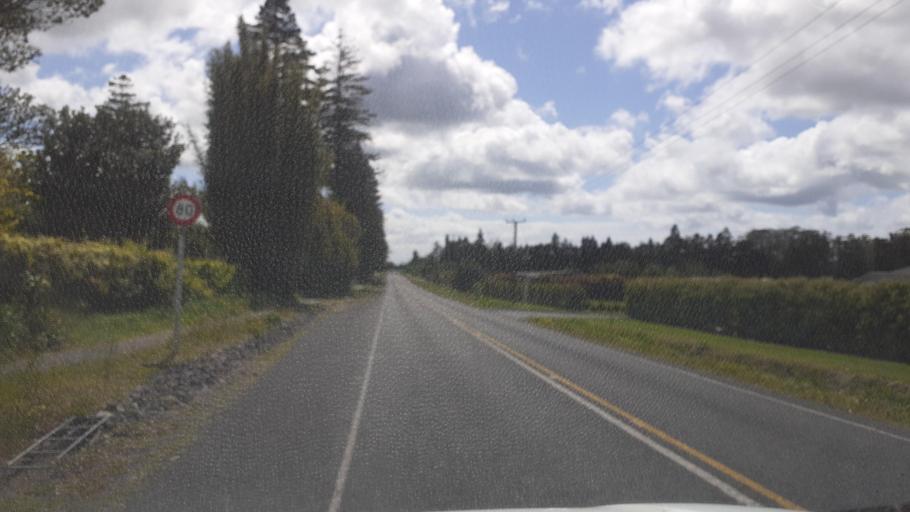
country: NZ
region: Northland
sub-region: Far North District
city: Kerikeri
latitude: -35.2265
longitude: 173.9693
